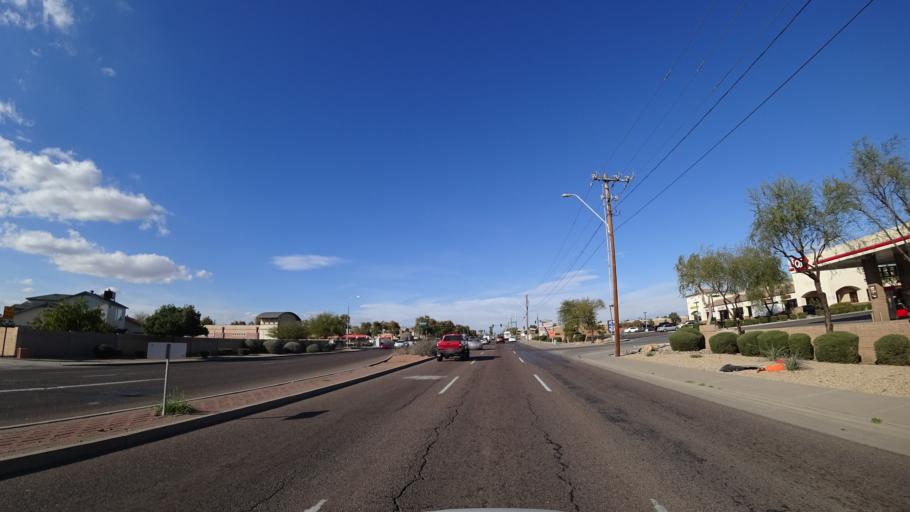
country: US
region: Arizona
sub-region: Maricopa County
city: Tolleson
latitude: 33.4712
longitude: -112.2378
